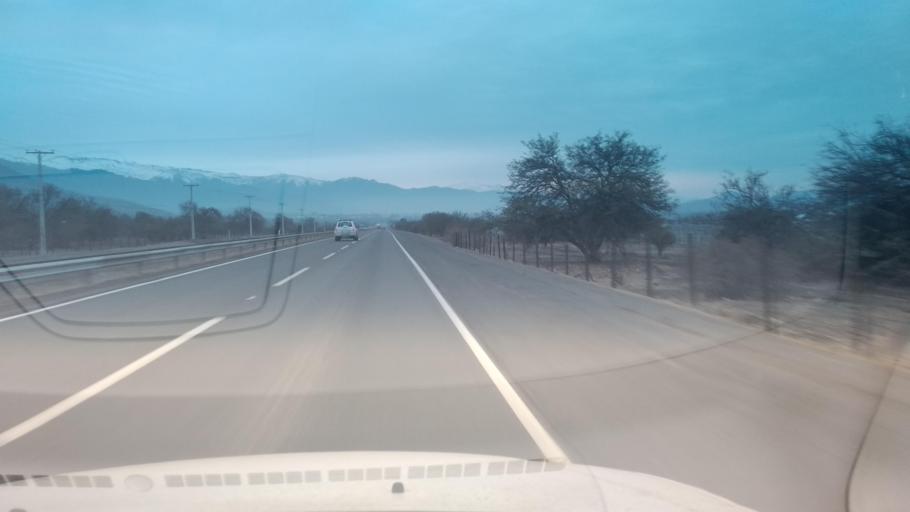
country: CL
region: Santiago Metropolitan
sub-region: Provincia de Chacabuco
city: Chicureo Abajo
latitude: -33.1123
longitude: -70.6855
